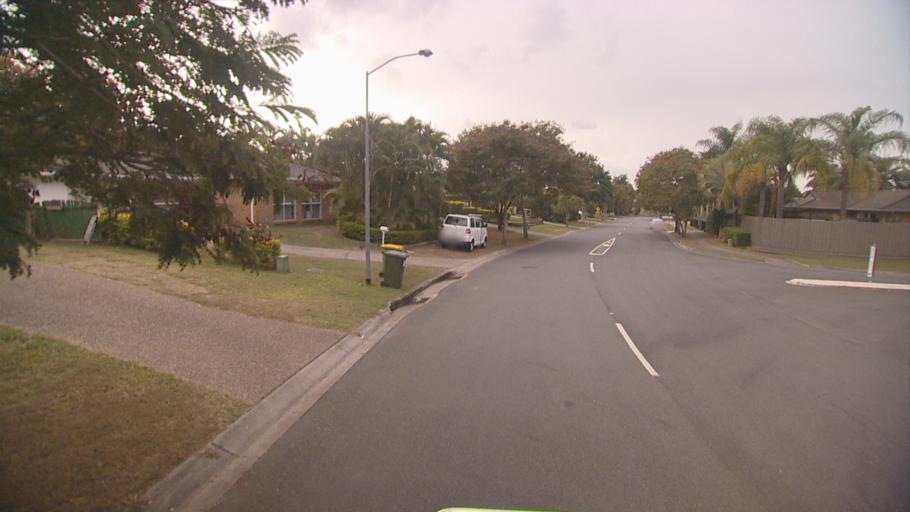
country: AU
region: Queensland
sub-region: Logan
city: Park Ridge South
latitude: -27.6765
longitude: 153.0203
